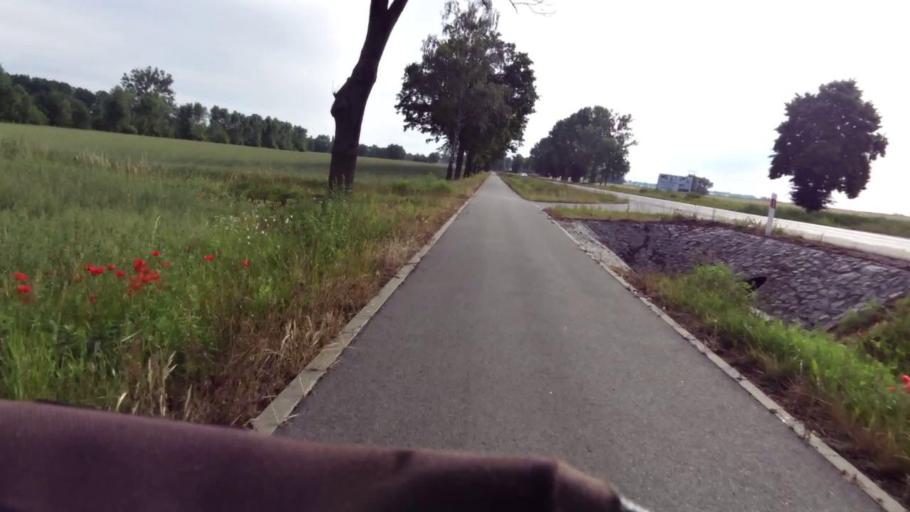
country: PL
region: West Pomeranian Voivodeship
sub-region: Powiat kamienski
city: Kamien Pomorski
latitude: 53.9907
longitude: 14.8101
